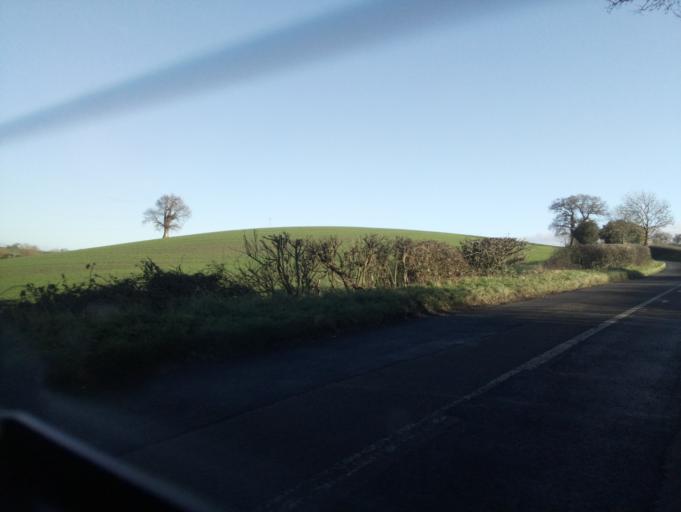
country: GB
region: England
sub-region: Staffordshire
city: Barton under Needwood
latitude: 52.8194
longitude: -1.7749
